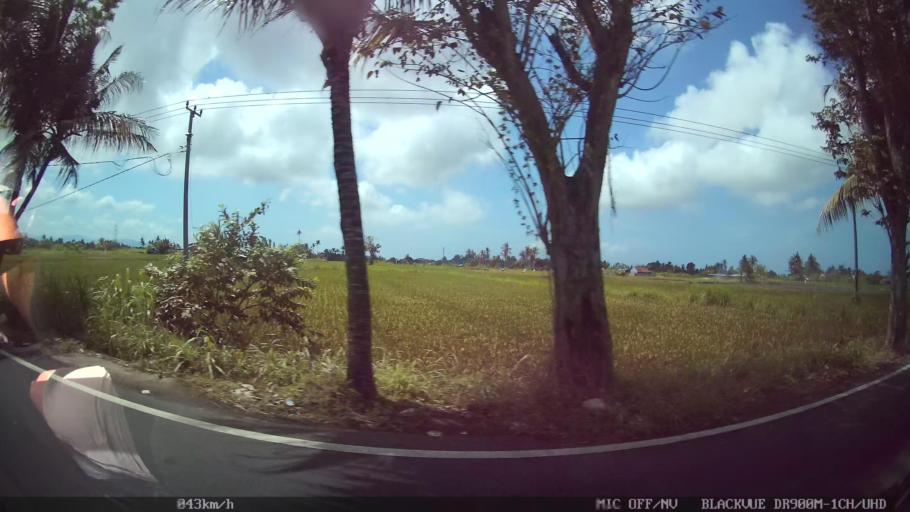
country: ID
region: Bali
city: Banjar Desa
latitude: -8.5785
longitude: 115.2957
